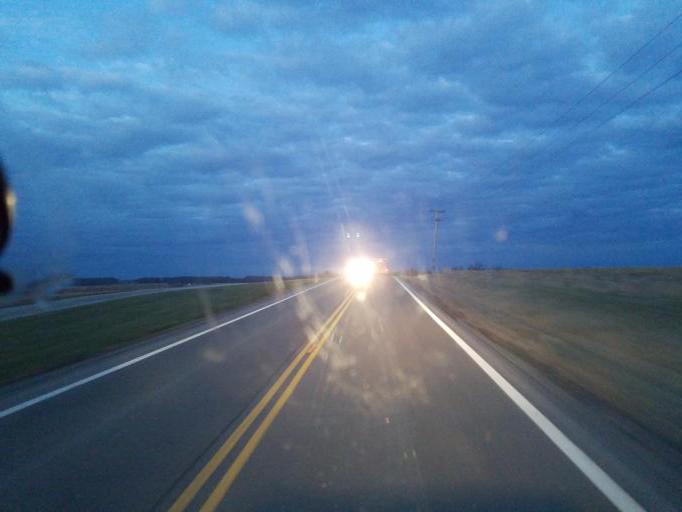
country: US
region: Ohio
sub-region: Knox County
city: Gambier
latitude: 40.3318
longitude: -82.3036
